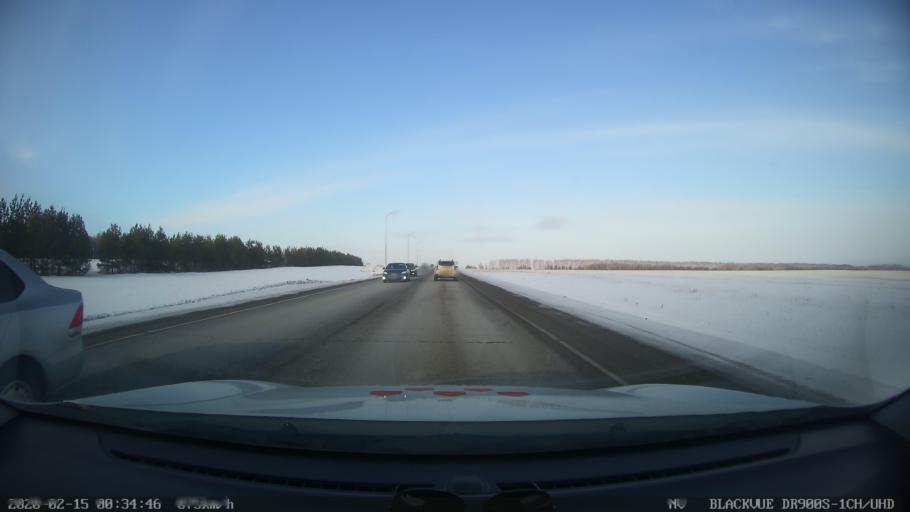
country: RU
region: Tatarstan
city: Verkhniy Uslon
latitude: 55.7021
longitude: 48.8879
